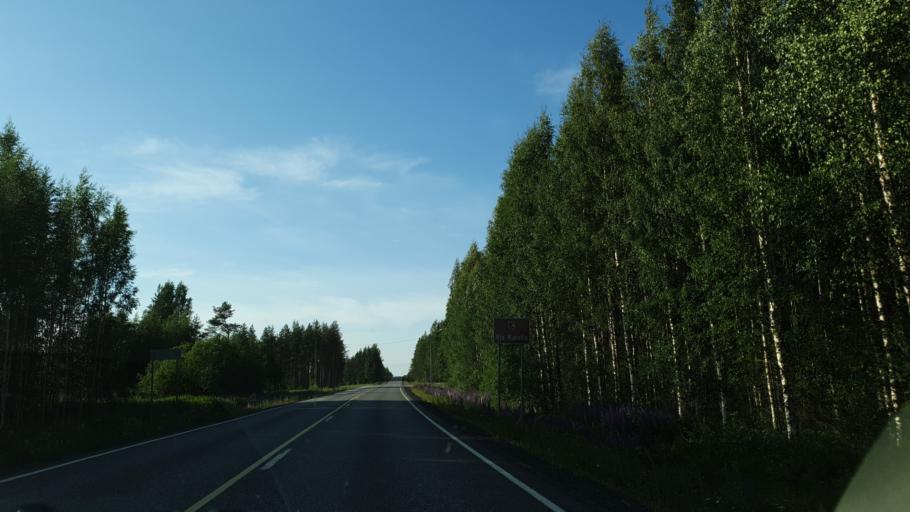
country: FI
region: Kainuu
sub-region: Kehys-Kainuu
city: Kuhmo
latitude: 64.0798
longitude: 29.4863
